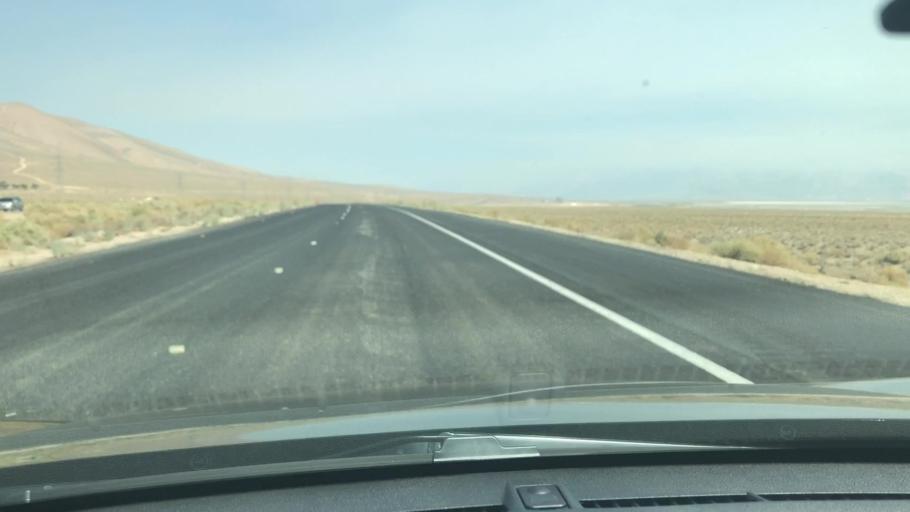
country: US
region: California
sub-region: Inyo County
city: Lone Pine
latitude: 36.4320
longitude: -118.0317
